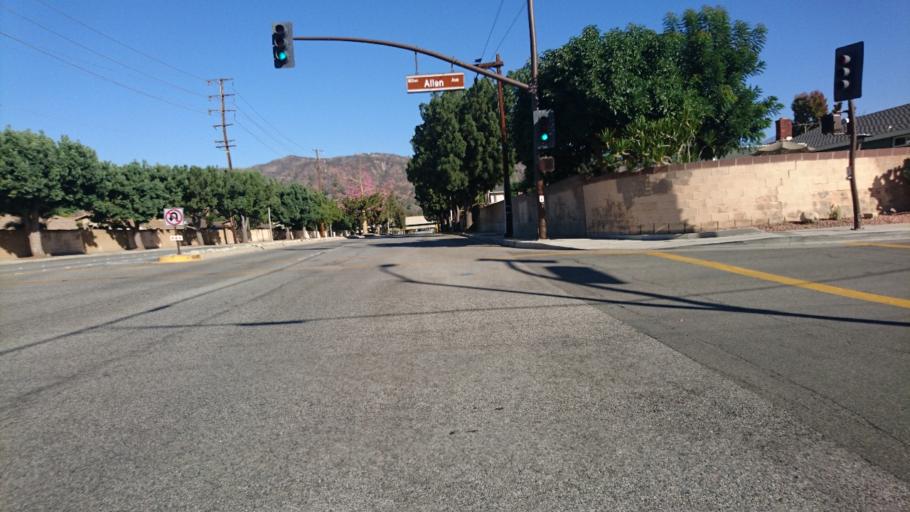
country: US
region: California
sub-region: Los Angeles County
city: San Dimas
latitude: 34.1175
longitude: -117.7939
